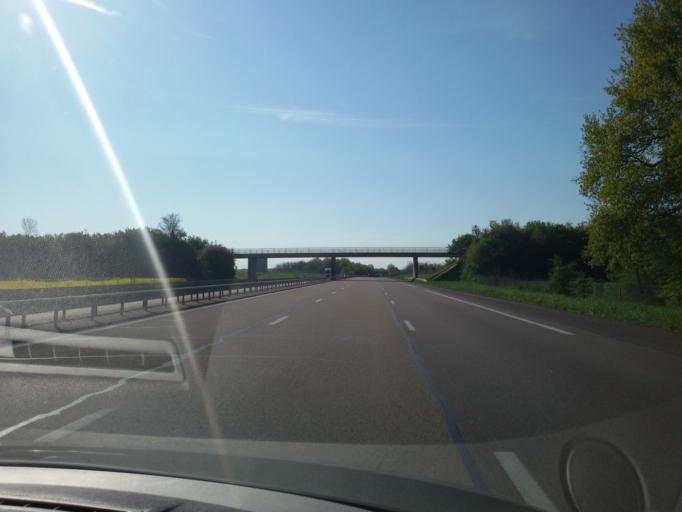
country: FR
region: Centre
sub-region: Departement du Loiret
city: Courtenay
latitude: 48.0028
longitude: 3.1636
